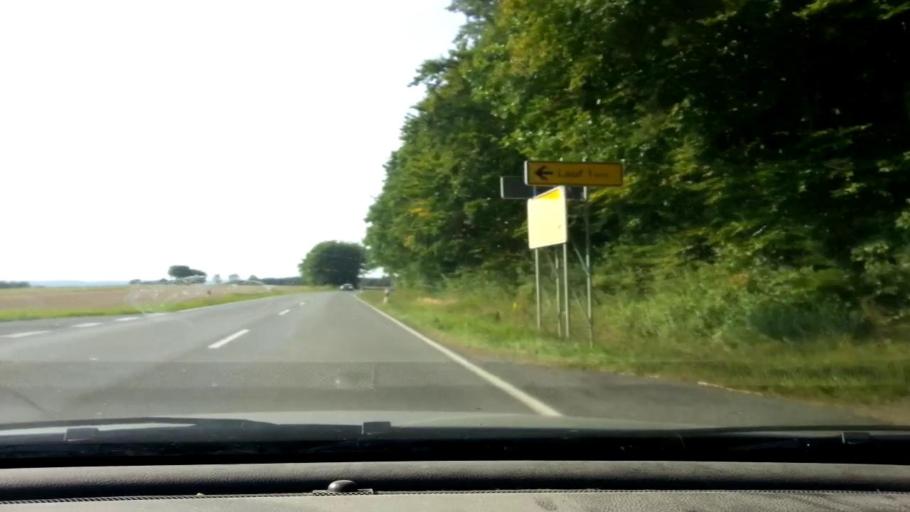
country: DE
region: Bavaria
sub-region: Upper Franconia
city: Zapfendorf
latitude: 50.0031
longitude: 10.9531
